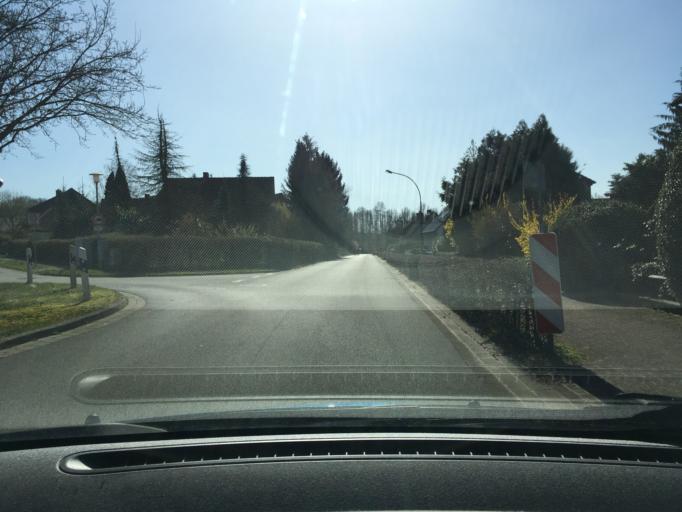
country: DE
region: Lower Saxony
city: Ebstorf
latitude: 53.0218
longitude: 10.4068
